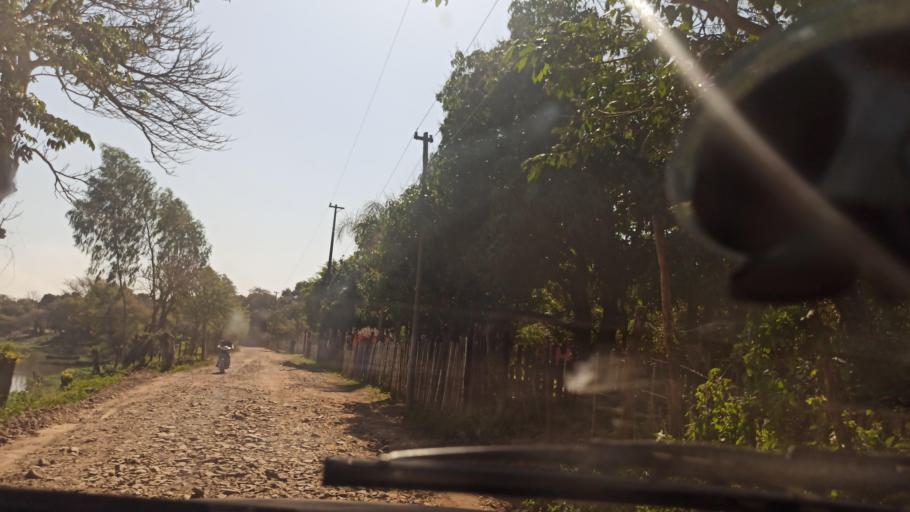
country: AR
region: Formosa
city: Clorinda
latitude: -25.3021
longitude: -57.7029
